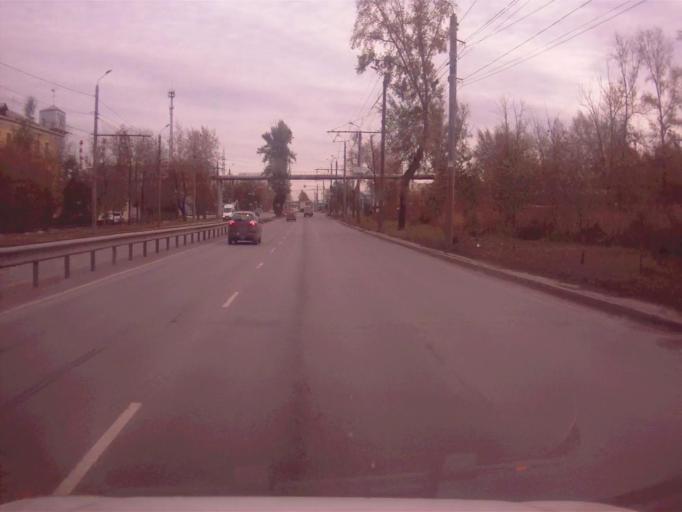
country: RU
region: Chelyabinsk
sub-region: Gorod Chelyabinsk
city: Chelyabinsk
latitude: 55.1350
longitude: 61.4657
